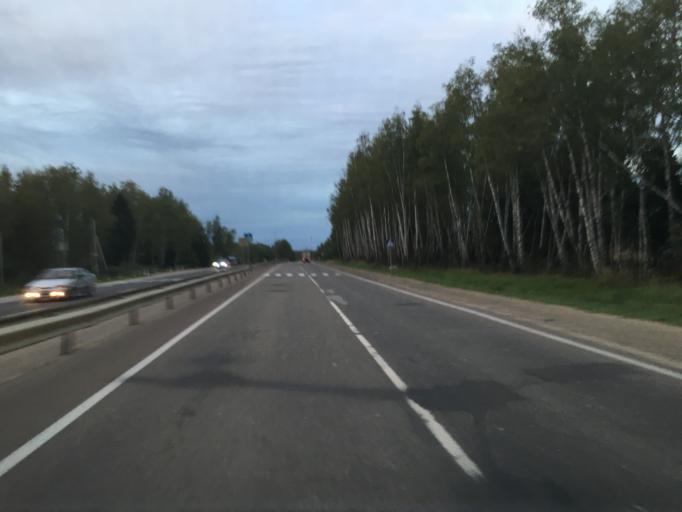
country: RU
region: Kaluga
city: Kaluga
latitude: 54.6338
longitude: 36.2955
